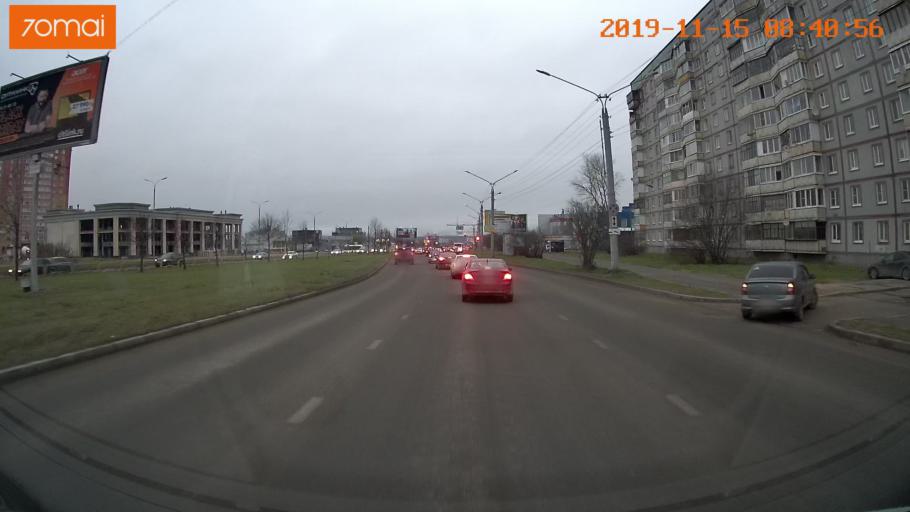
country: RU
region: Vologda
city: Cherepovets
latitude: 59.0966
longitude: 37.9126
